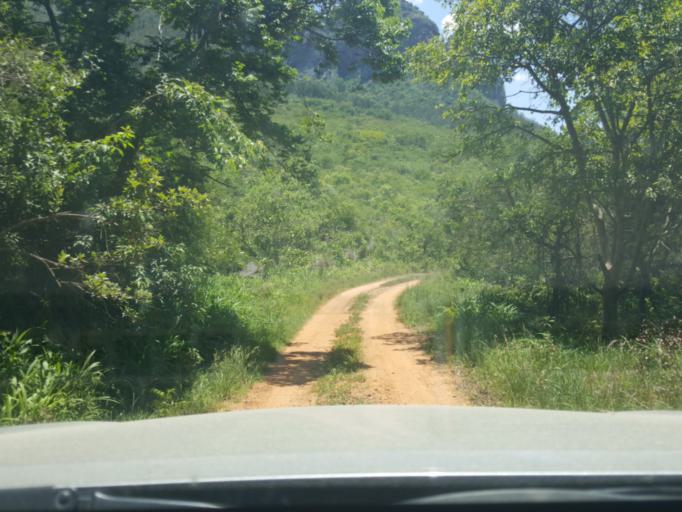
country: ZA
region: Limpopo
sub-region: Mopani District Municipality
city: Hoedspruit
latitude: -24.5973
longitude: 30.8531
